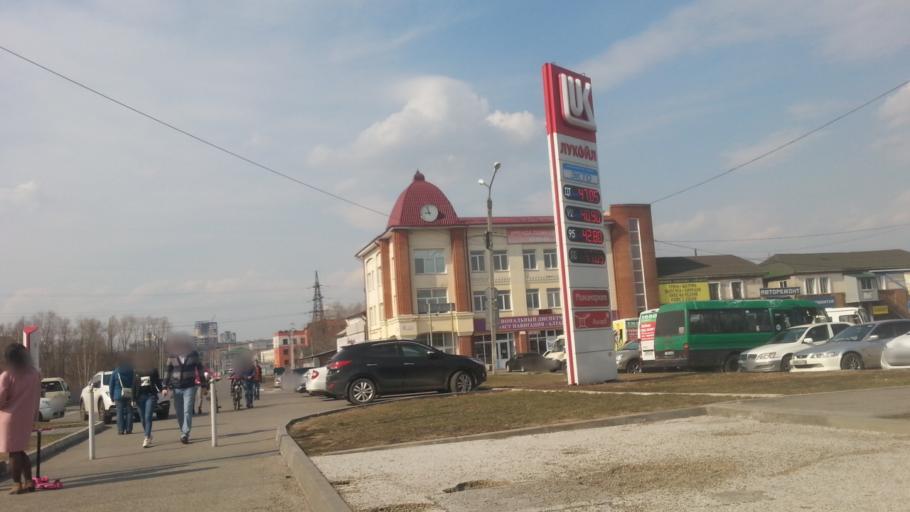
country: RU
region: Altai Krai
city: Zaton
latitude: 53.3263
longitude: 83.7933
